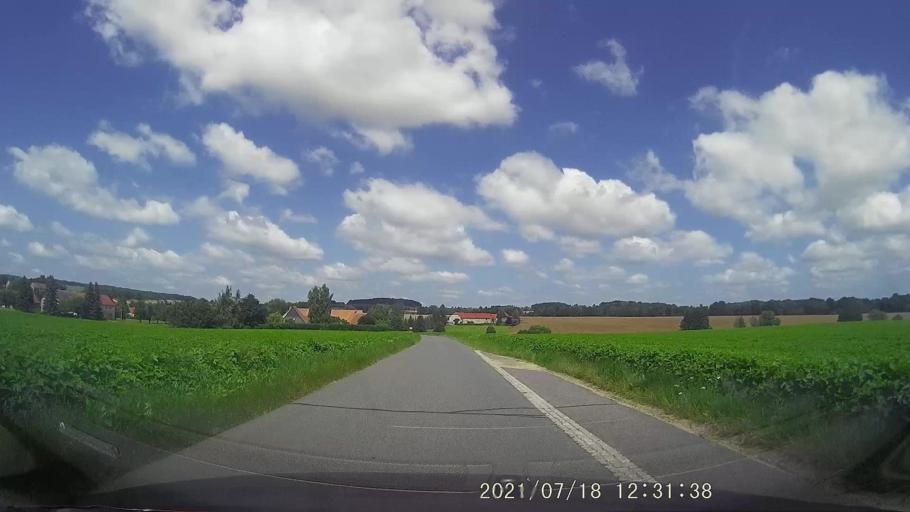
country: DE
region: Saxony
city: Konigshain
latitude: 51.1781
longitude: 14.8975
